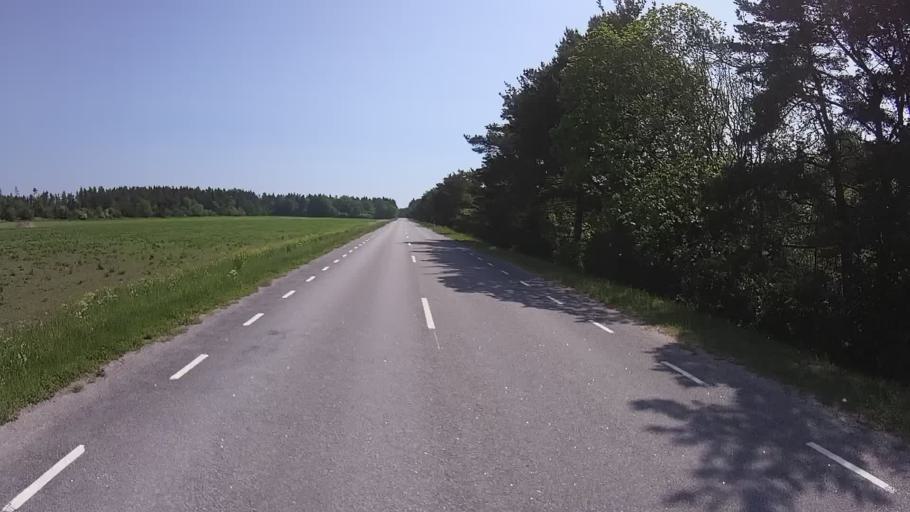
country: EE
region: Saare
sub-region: Kuressaare linn
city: Kuressaare
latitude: 58.3609
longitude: 22.0609
